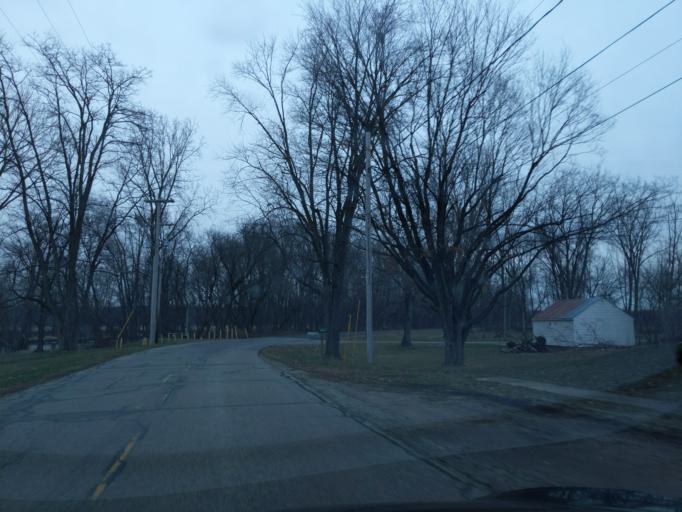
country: US
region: Michigan
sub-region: Ionia County
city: Portland
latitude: 42.9856
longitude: -84.9445
